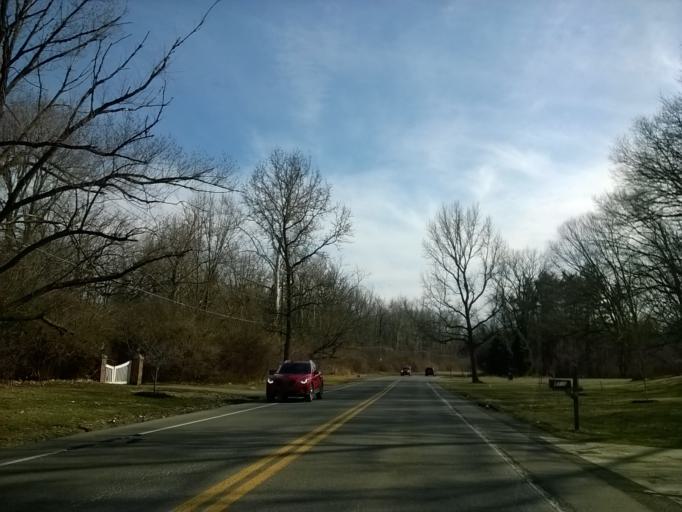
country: US
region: Indiana
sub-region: Marion County
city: Speedway
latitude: 39.8395
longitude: -86.2118
